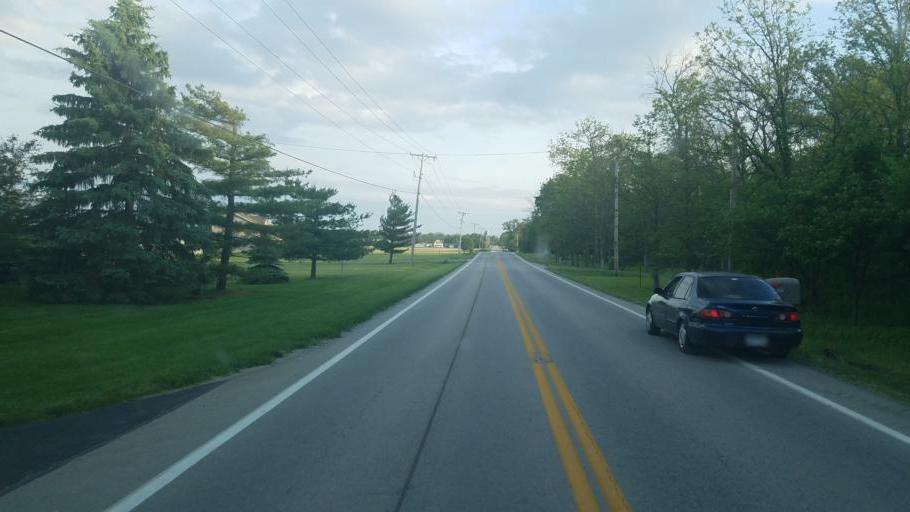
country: US
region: Ohio
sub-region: Clinton County
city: Sabina
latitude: 39.4676
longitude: -83.6656
